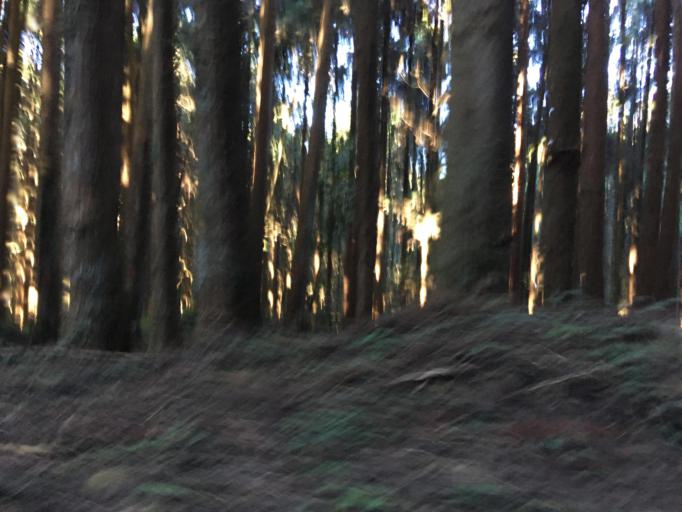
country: TW
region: Taiwan
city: Lugu
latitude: 23.5140
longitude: 120.8005
